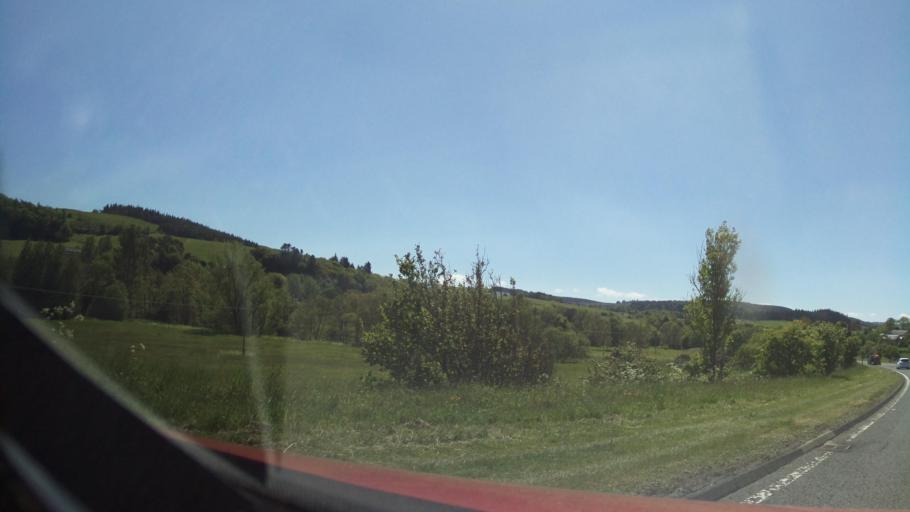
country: GB
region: Scotland
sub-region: The Scottish Borders
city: Selkirk
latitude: 55.4967
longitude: -2.8336
